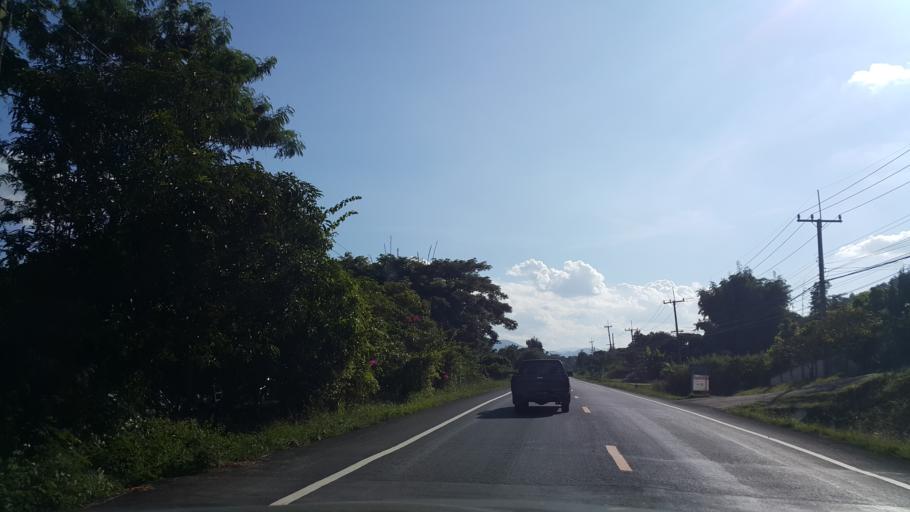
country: TH
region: Lamphun
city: Mae Tha
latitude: 18.4993
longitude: 99.1963
